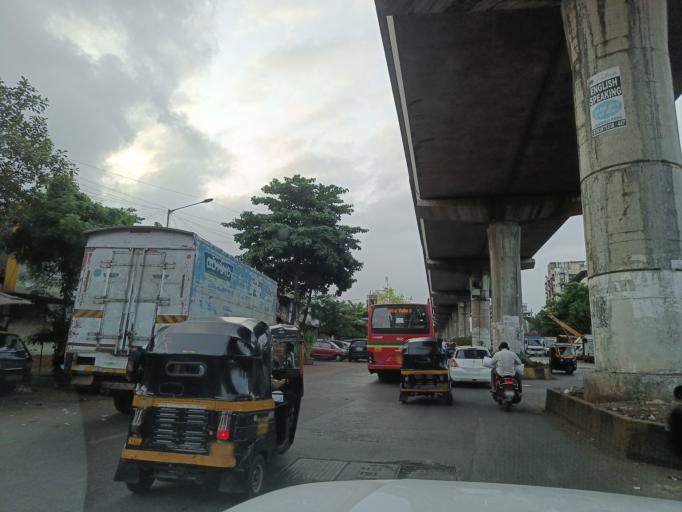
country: IN
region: Maharashtra
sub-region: Mumbai Suburban
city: Powai
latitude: 19.0959
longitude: 72.8956
